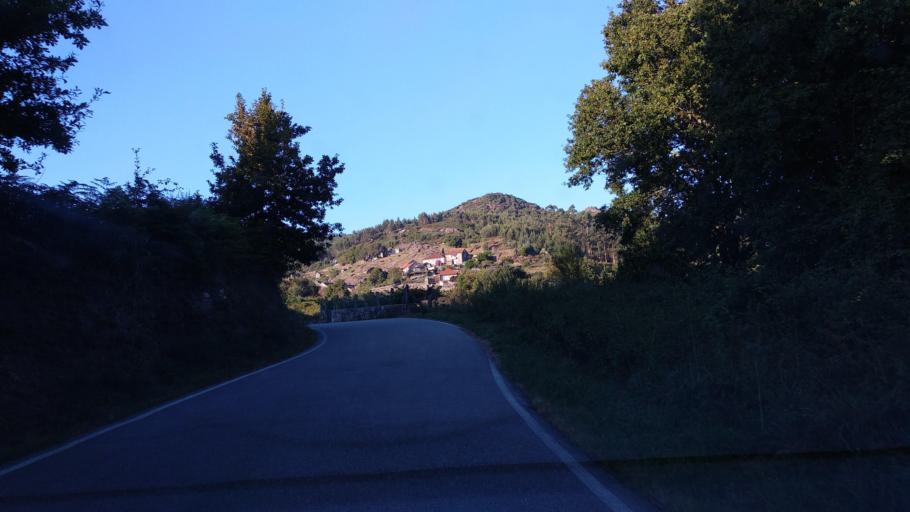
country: ES
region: Galicia
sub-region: Provincia de Pontevedra
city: Ponte Caldelas
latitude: 42.3555
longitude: -8.4914
